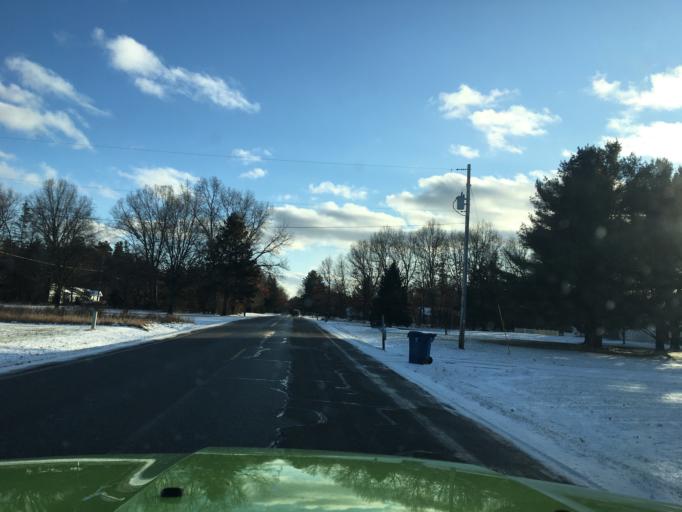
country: US
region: Michigan
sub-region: Montcalm County
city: Greenville
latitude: 43.2036
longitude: -85.2826
